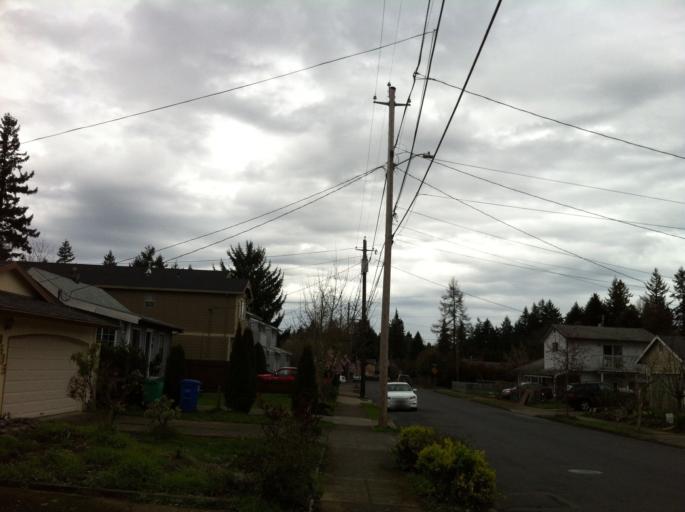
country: US
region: Oregon
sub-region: Multnomah County
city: Lents
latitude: 45.5350
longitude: -122.5757
